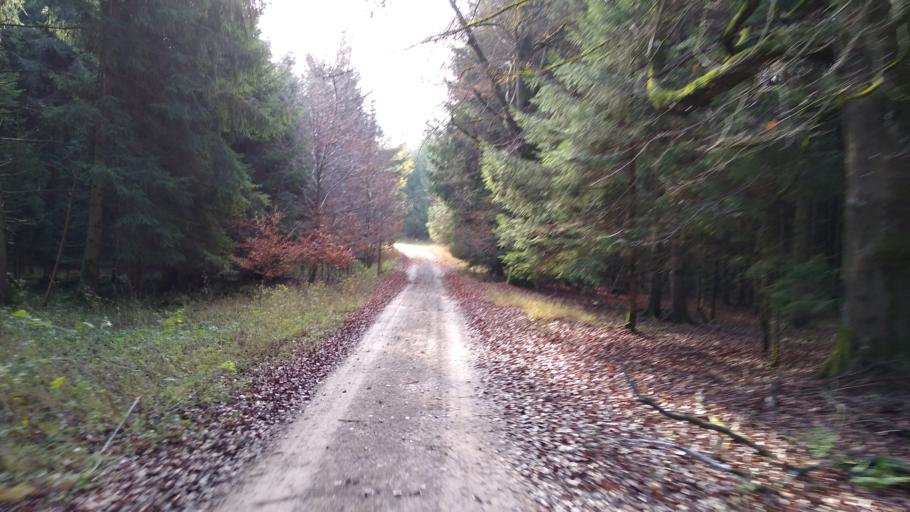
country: DE
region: Bavaria
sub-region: Upper Palatinate
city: Seubersdorf
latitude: 49.1364
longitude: 11.6326
